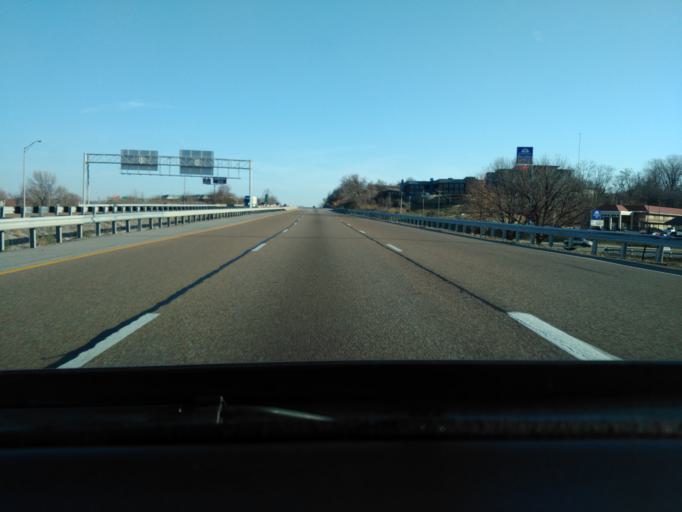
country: US
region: Illinois
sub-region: Madison County
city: Collinsville
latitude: 38.6794
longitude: -90.0131
